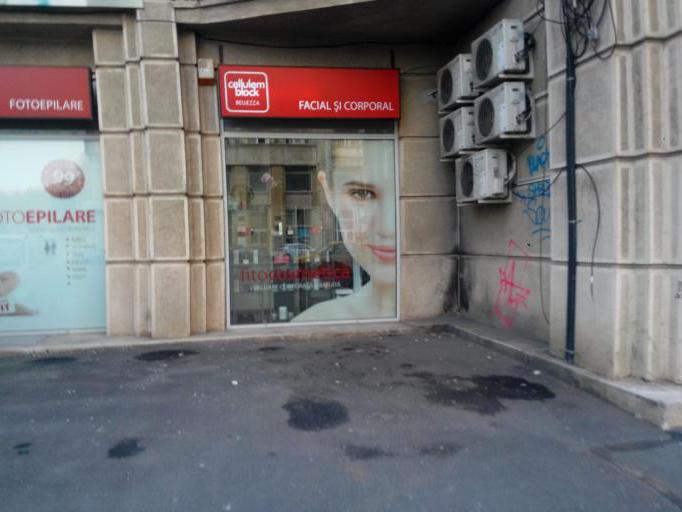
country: RO
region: Bucuresti
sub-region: Municipiul Bucuresti
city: Bucuresti
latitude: 44.4513
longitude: 26.0843
